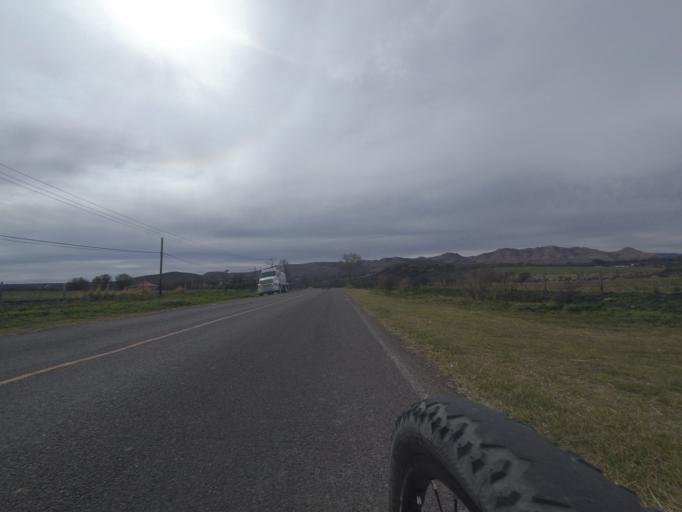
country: MX
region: Aguascalientes
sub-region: Aguascalientes
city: La Loma de los Negritos
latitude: 21.8369
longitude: -102.3618
